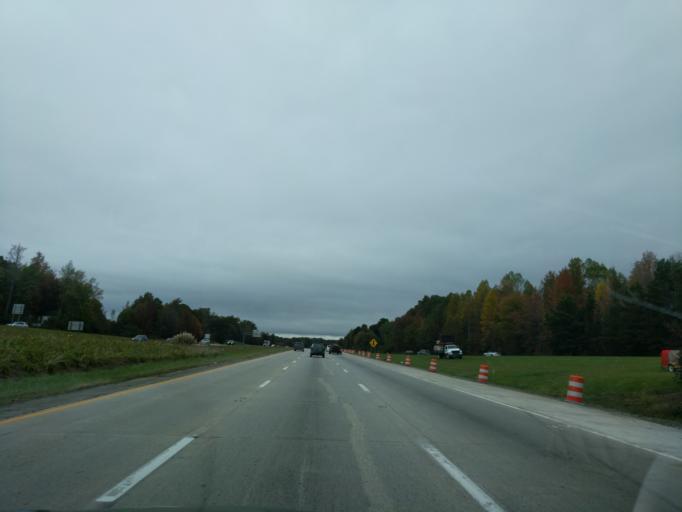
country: US
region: North Carolina
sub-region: Randolph County
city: Archdale
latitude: 35.9035
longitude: -79.9540
